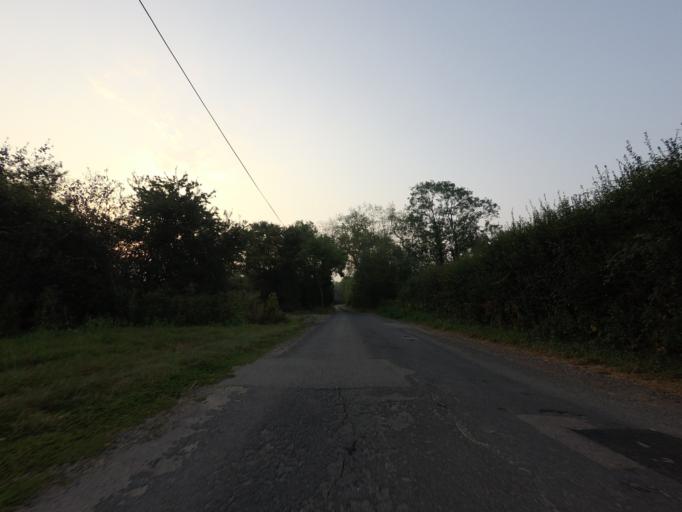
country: GB
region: England
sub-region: Kent
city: Headcorn
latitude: 51.1829
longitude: 0.6674
